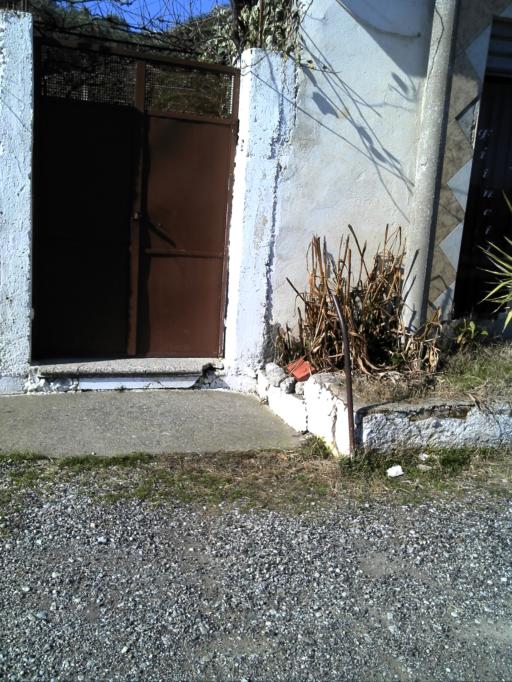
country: AL
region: Shkoder
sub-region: Rrethi i Shkodres
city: Berdica e Madhe
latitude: 42.0314
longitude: 19.4746
